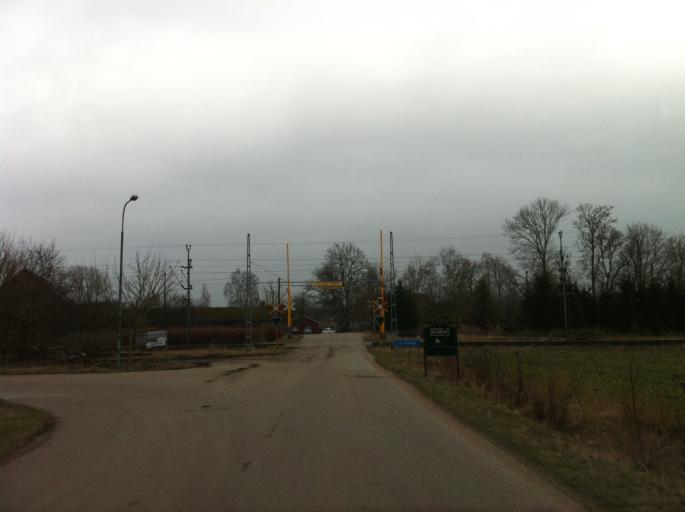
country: SE
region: Skane
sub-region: Landskrona
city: Asmundtorp
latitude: 55.9298
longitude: 13.0036
